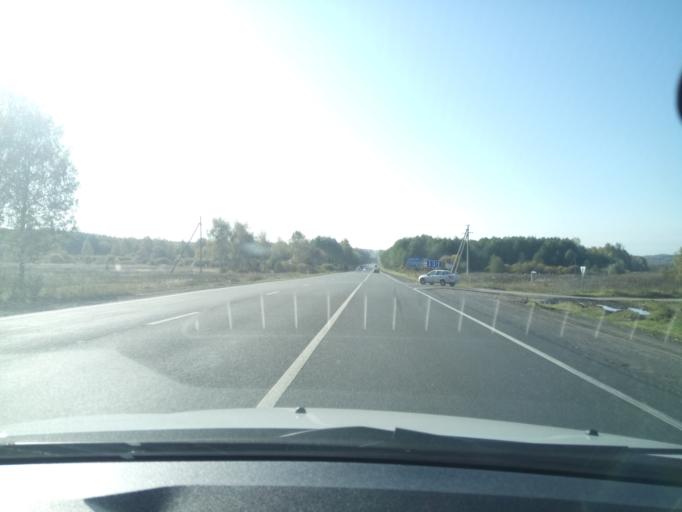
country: RU
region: Nizjnij Novgorod
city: Dal'neye Konstantinovo
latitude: 55.9891
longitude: 43.9699
